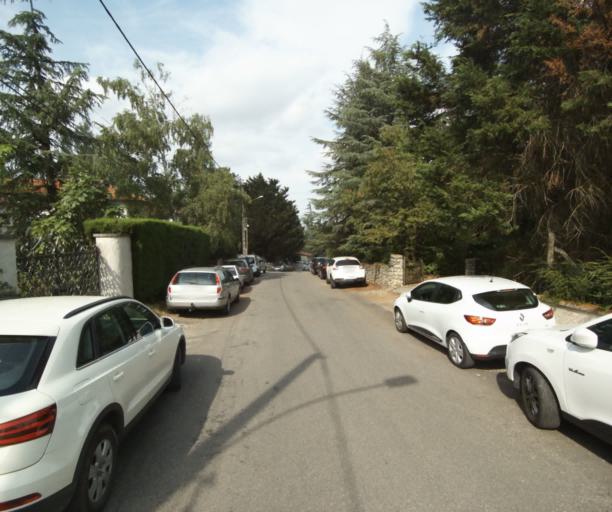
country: FR
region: Midi-Pyrenees
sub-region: Departement de la Haute-Garonne
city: Revel
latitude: 43.4418
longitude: 2.0249
